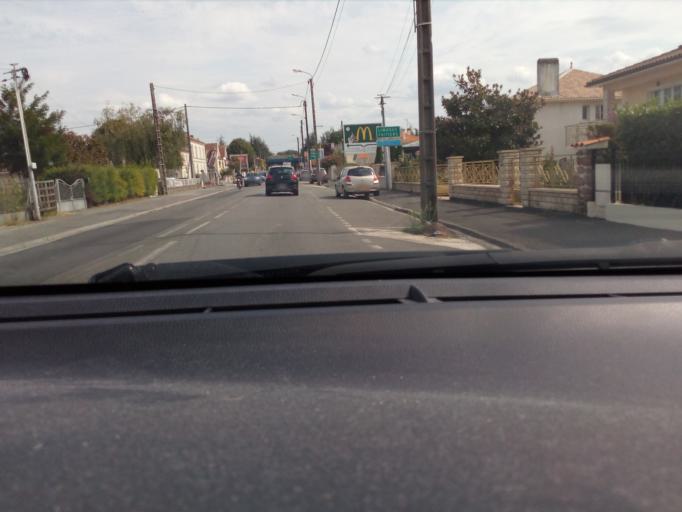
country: FR
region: Poitou-Charentes
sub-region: Departement de la Charente
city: Saint-Yrieix-sur-Charente
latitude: 45.6652
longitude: 0.1257
